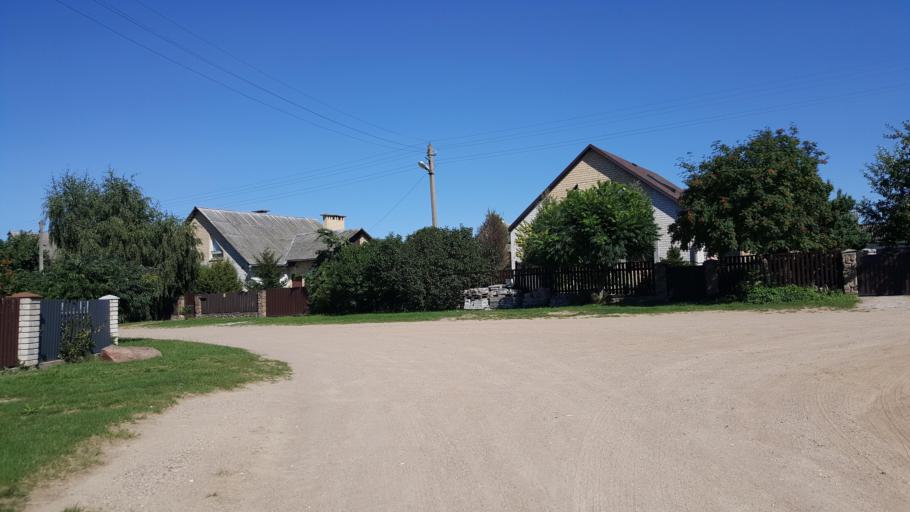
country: BY
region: Brest
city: Charnawchytsy
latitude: 52.2080
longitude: 23.7413
